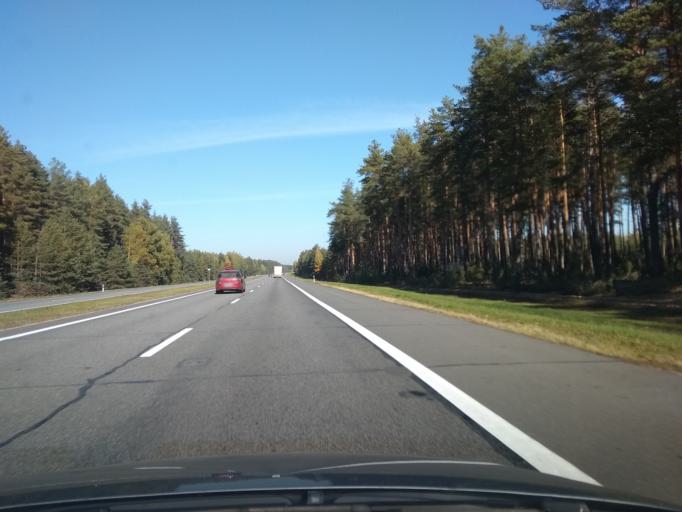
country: BY
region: Brest
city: Baranovichi
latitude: 52.9861
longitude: 25.7515
